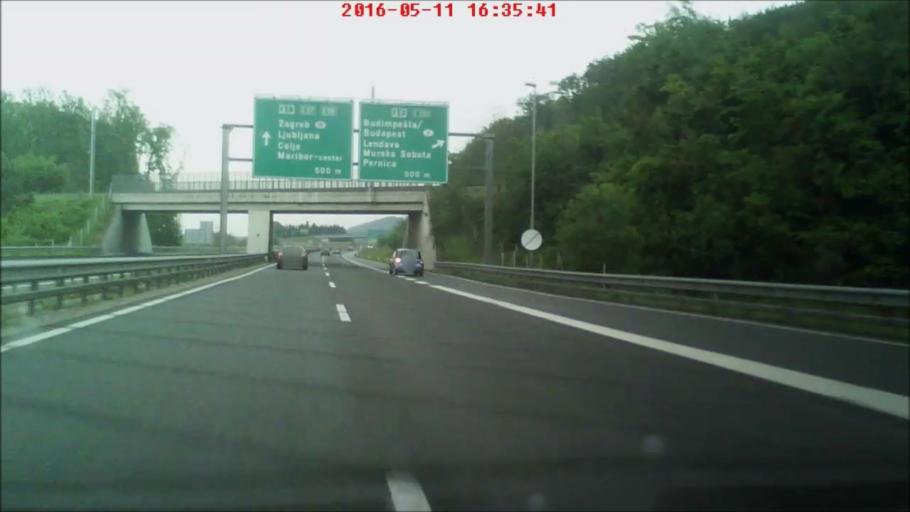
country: SI
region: Pesnica
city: Pesnica pri Mariboru
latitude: 46.5955
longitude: 15.6724
